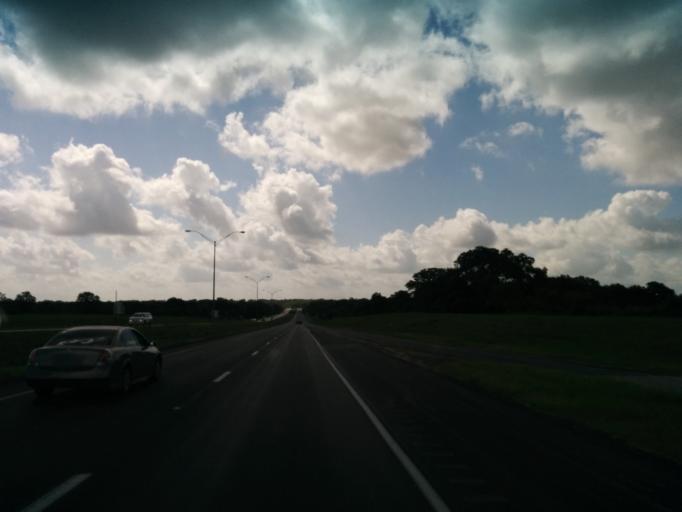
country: US
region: Texas
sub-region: Fayette County
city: Schulenburg
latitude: 29.6935
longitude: -96.8475
